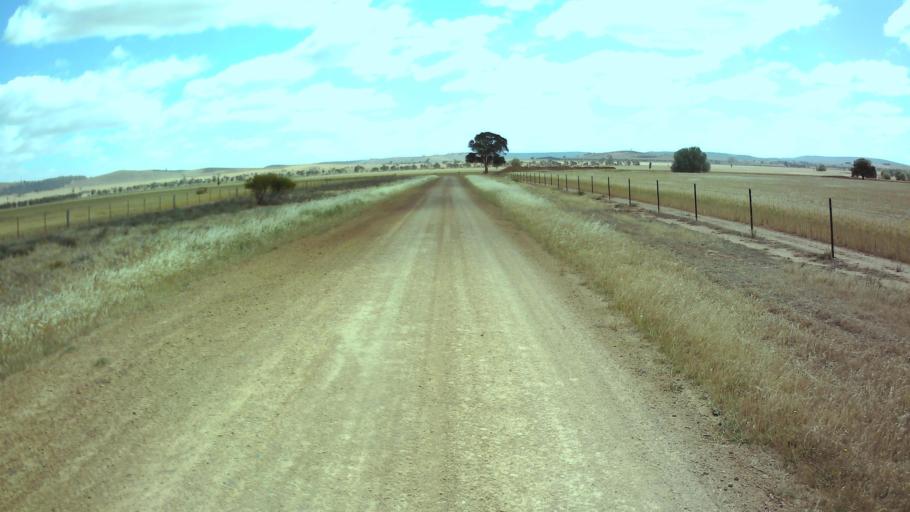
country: AU
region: New South Wales
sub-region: Weddin
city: Grenfell
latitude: -33.9974
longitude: 148.3017
